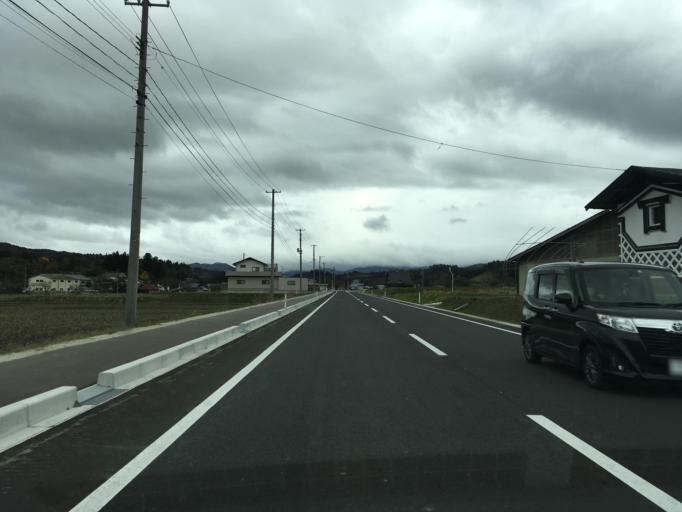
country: JP
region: Iwate
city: Ichinoseki
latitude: 39.0185
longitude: 141.3352
